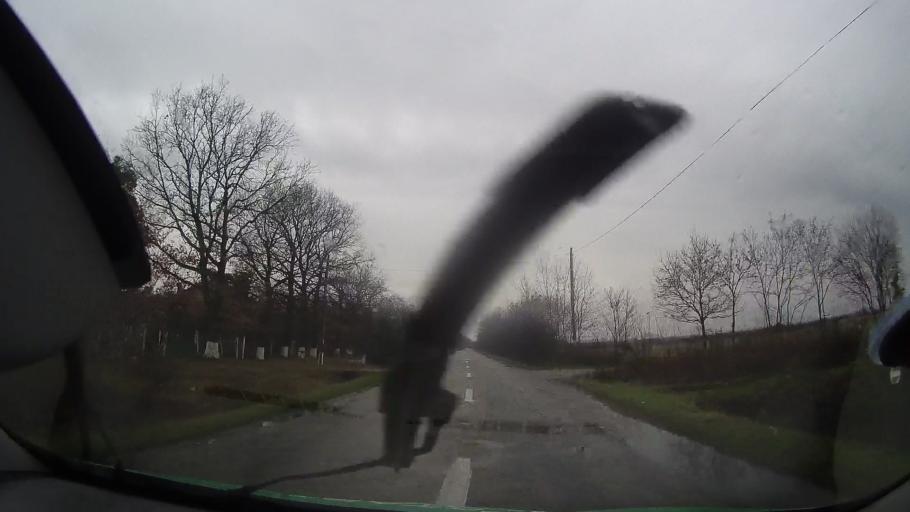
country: RO
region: Bihor
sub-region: Comuna Cociuba Mare
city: Cociuba Mare
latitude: 46.7424
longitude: 21.9748
